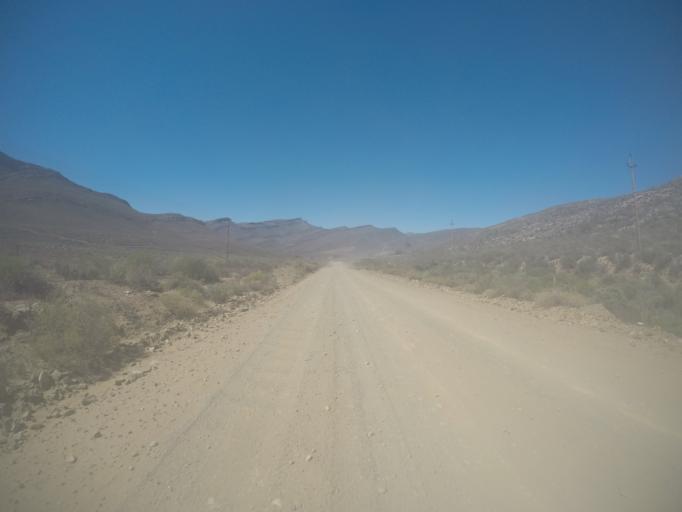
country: ZA
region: Western Cape
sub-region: West Coast District Municipality
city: Clanwilliam
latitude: -32.5460
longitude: 19.3588
